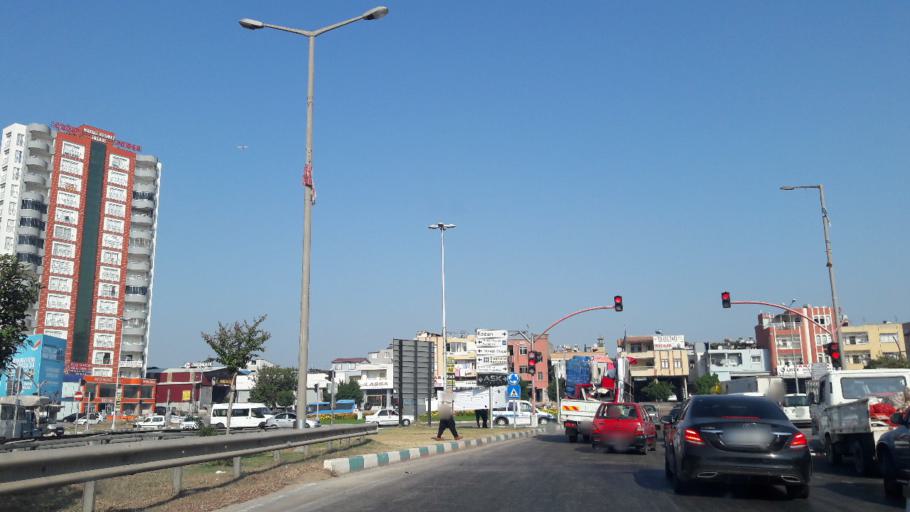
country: TR
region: Adana
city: Yuregir
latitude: 37.0246
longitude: 35.3998
